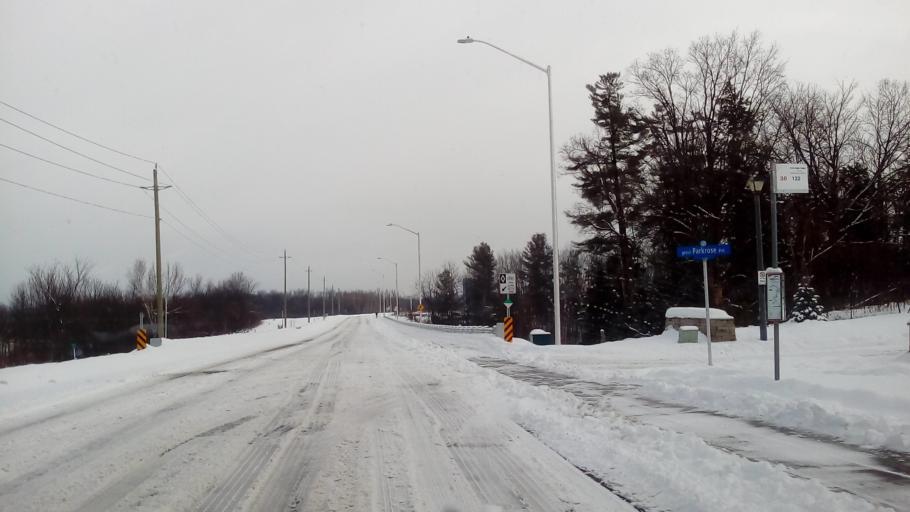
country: CA
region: Quebec
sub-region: Outaouais
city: Gatineau
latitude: 45.4933
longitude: -75.4939
